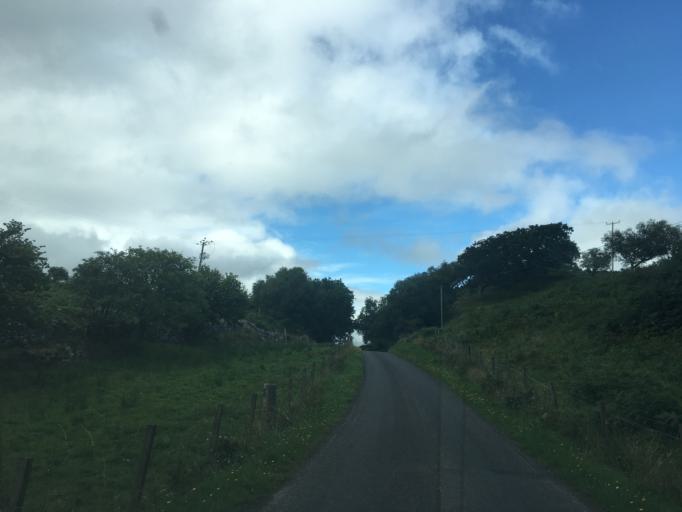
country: GB
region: Scotland
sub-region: Argyll and Bute
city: Ardrishaig
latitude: 56.0869
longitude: -5.5604
